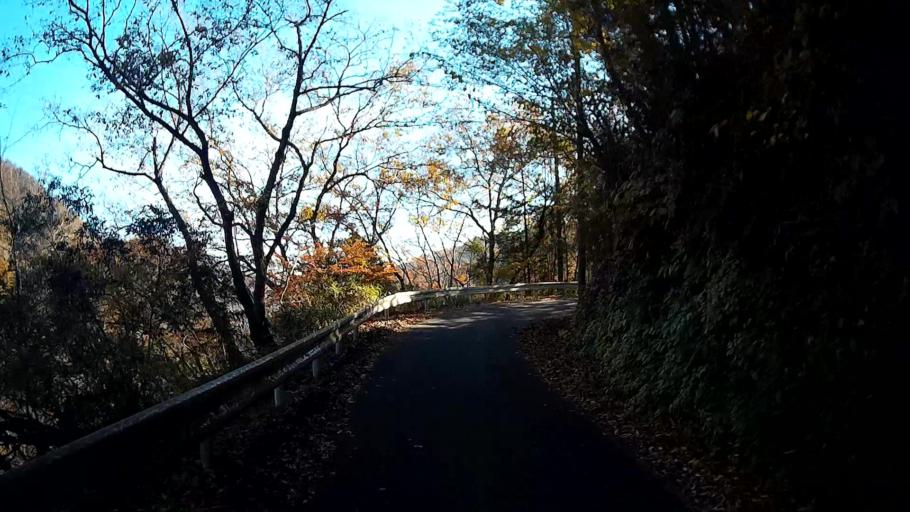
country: JP
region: Yamanashi
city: Uenohara
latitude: 35.5927
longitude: 139.1294
